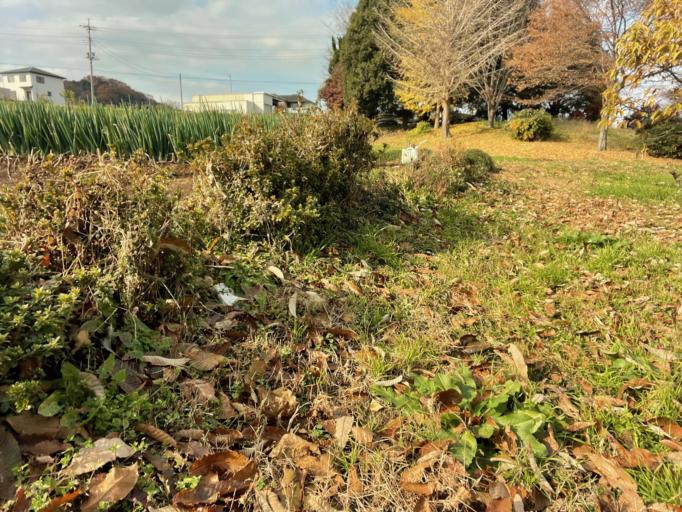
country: JP
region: Saitama
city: Yorii
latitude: 36.1448
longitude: 139.1931
